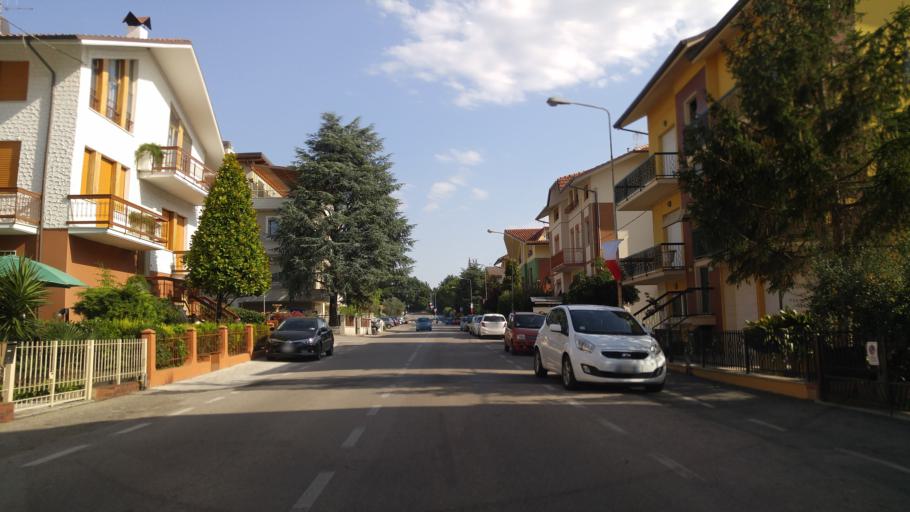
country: IT
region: The Marches
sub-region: Provincia di Pesaro e Urbino
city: Pesaro
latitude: 43.8956
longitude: 12.9241
